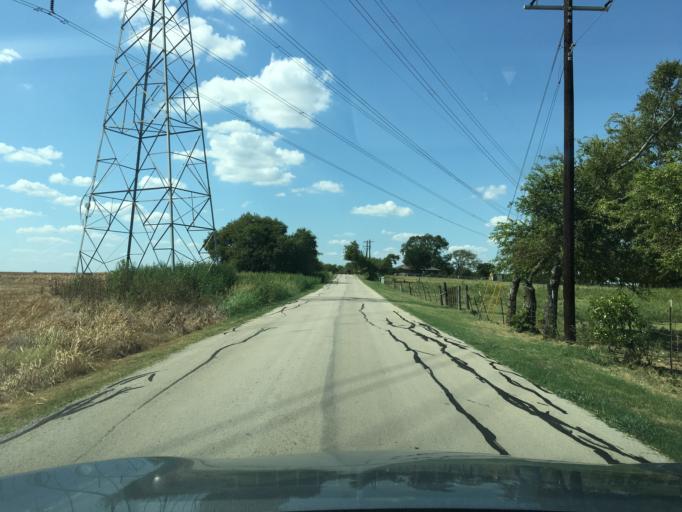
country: US
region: Texas
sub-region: Tarrant County
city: Mansfield
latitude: 32.5209
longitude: -97.0759
